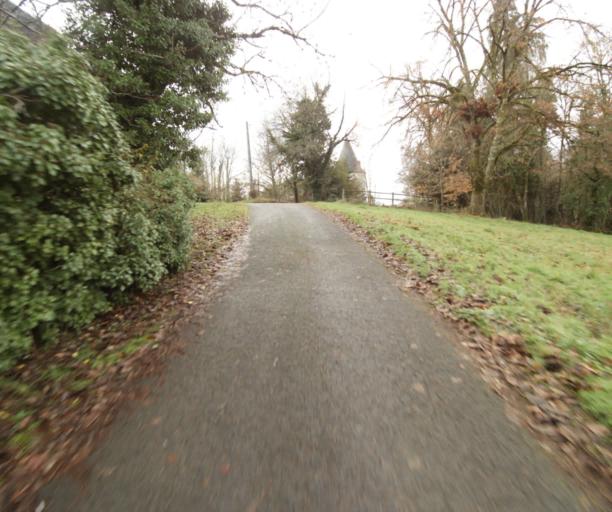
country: FR
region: Limousin
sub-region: Departement de la Correze
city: Saint-Mexant
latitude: 45.2748
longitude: 1.6405
